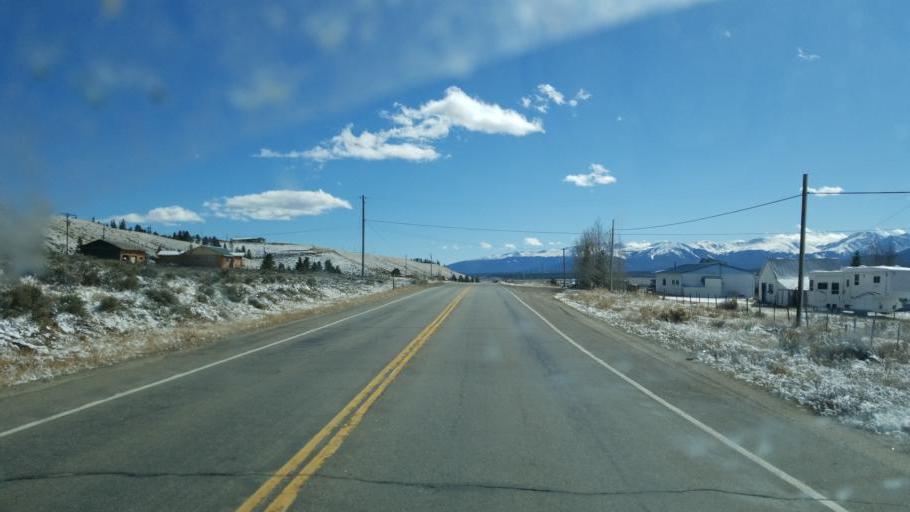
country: US
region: Colorado
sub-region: Lake County
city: Leadville North
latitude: 39.2183
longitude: -106.3480
